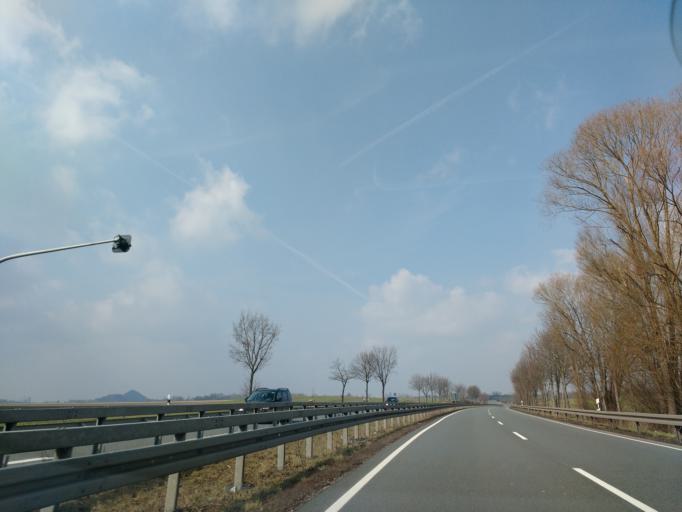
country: DE
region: Saxony-Anhalt
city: Bennstedt
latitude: 51.4770
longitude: 11.8216
